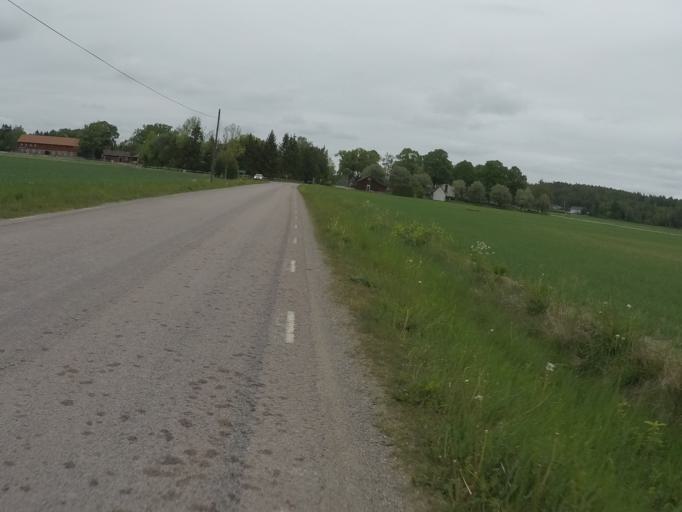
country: SE
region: Vaestmanland
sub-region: Hallstahammars Kommun
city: Kolback
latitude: 59.5460
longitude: 16.3107
